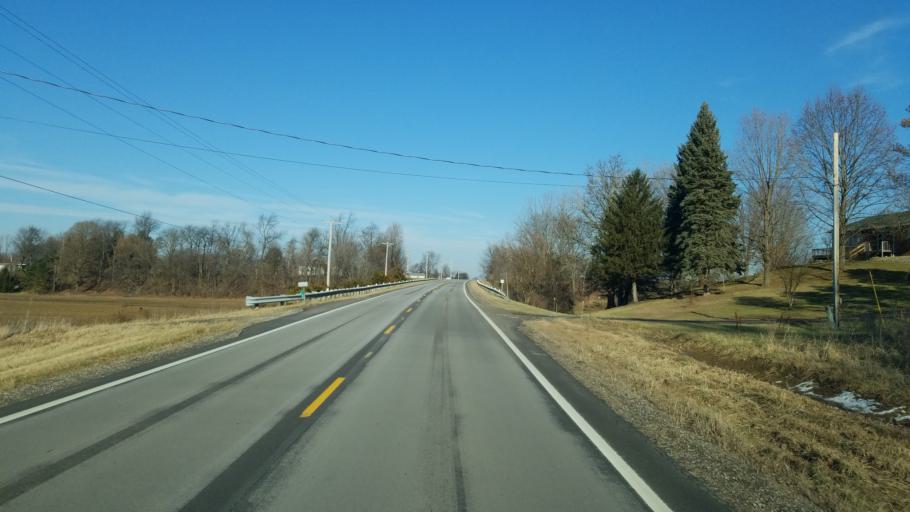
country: US
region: Ohio
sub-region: Huron County
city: Norwalk
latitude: 41.1725
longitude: -82.6444
